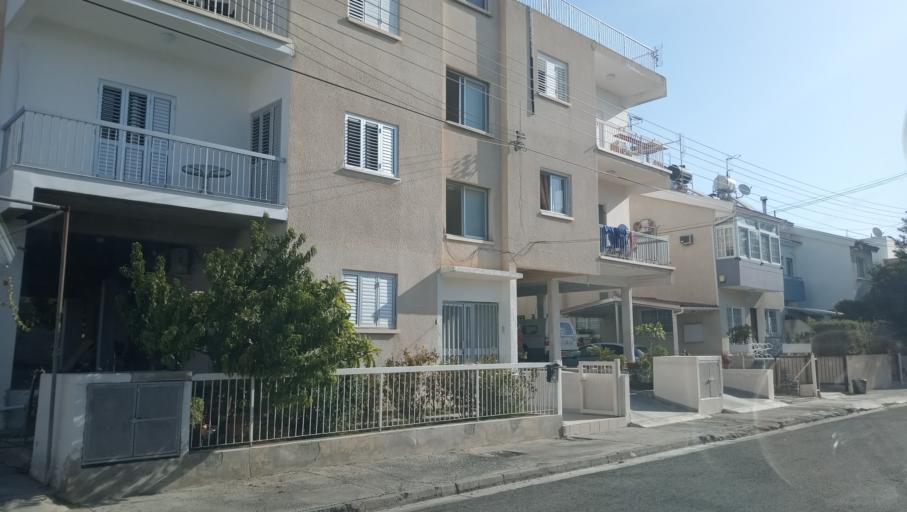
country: CY
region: Lefkosia
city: Nicosia
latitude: 35.1468
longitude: 33.3986
